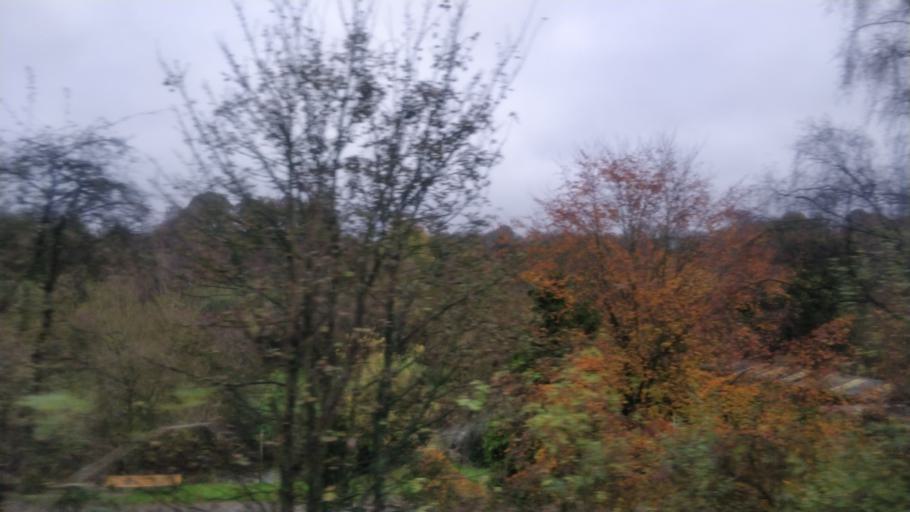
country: GB
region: England
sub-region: Borough of Wigan
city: Shevington
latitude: 53.5606
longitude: -2.6981
